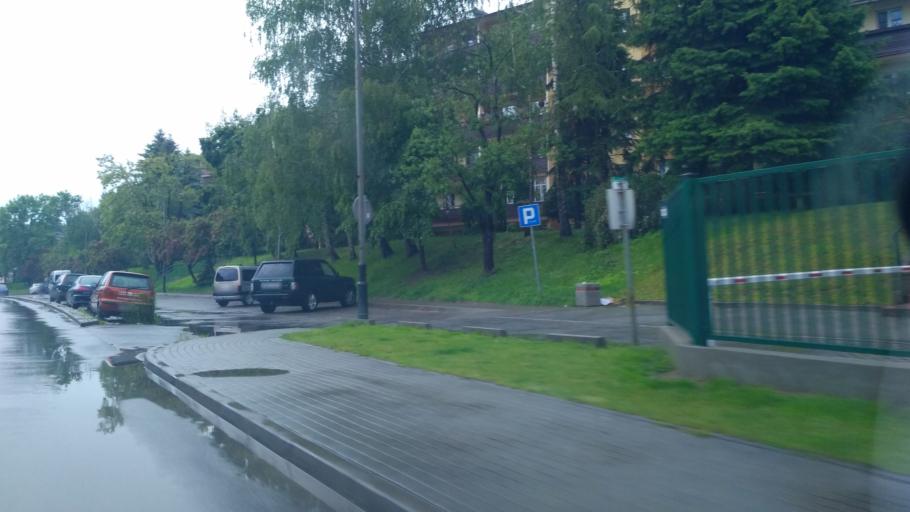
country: PL
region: Subcarpathian Voivodeship
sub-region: Powiat jasielski
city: Jaslo
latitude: 49.7463
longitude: 21.4687
